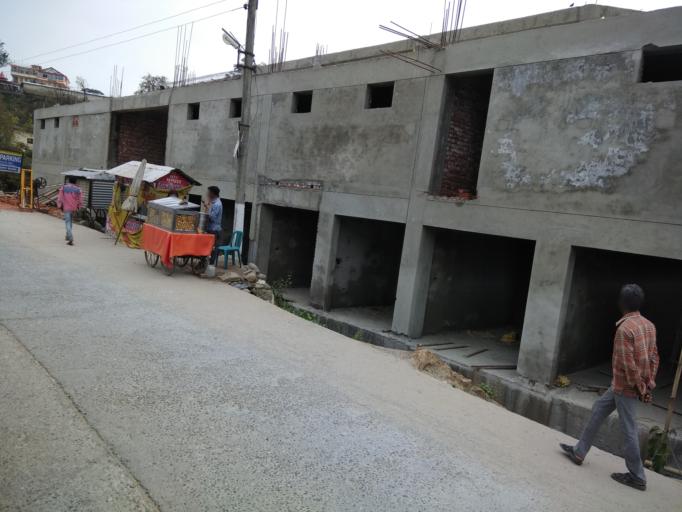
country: IN
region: Himachal Pradesh
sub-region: Kangra
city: Dharmsala
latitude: 32.1490
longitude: 76.4202
